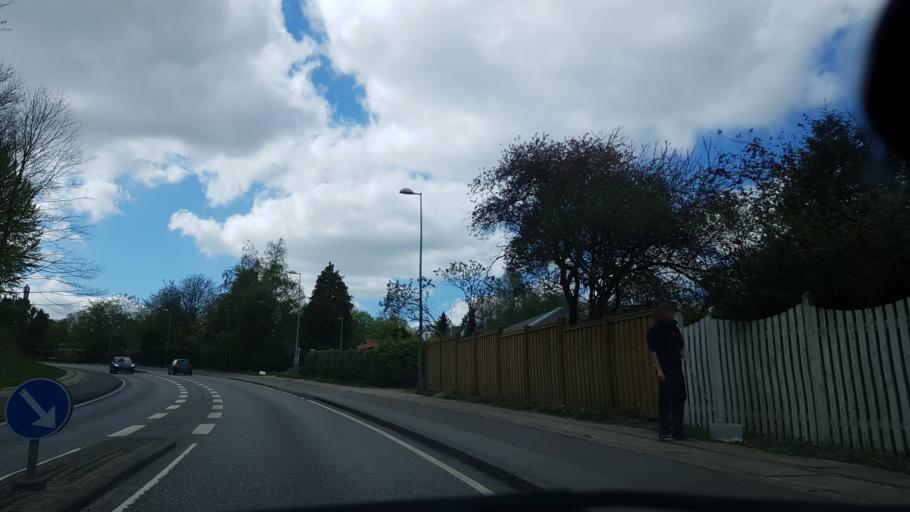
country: DK
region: Capital Region
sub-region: Horsholm Kommune
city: Horsholm
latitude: 55.8830
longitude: 12.5201
